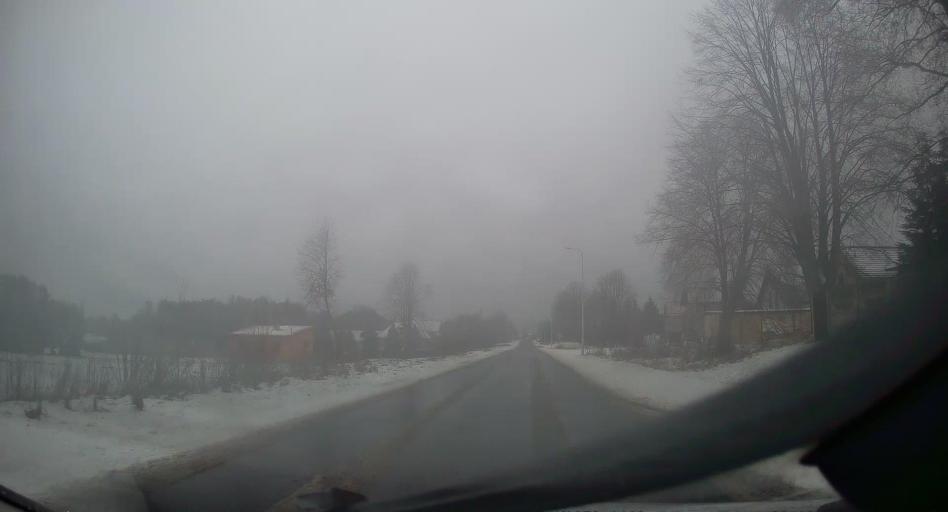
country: PL
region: Lodz Voivodeship
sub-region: Powiat rawski
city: Rawa Mazowiecka
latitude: 51.7047
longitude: 20.2133
